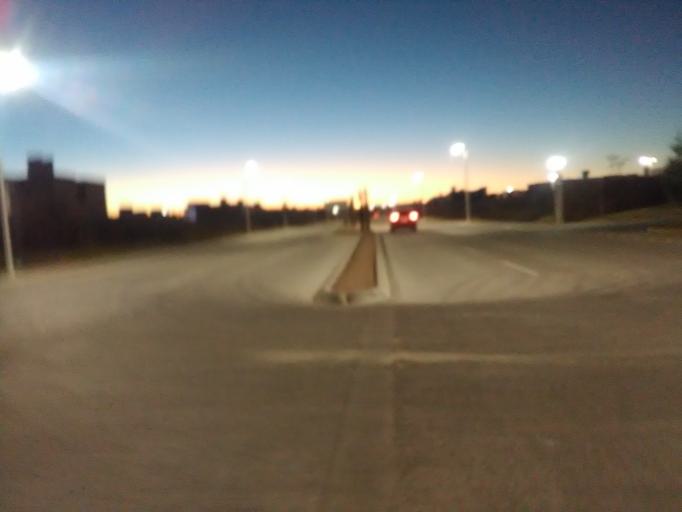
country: MX
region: Durango
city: Victoria de Durango
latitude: 24.0000
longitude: -104.6340
